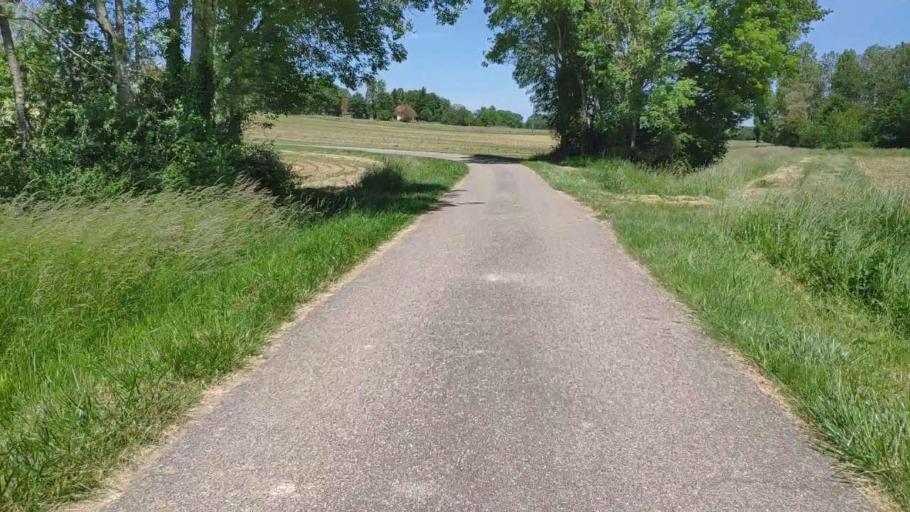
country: FR
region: Franche-Comte
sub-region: Departement du Jura
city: Bletterans
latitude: 46.7970
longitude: 5.3889
